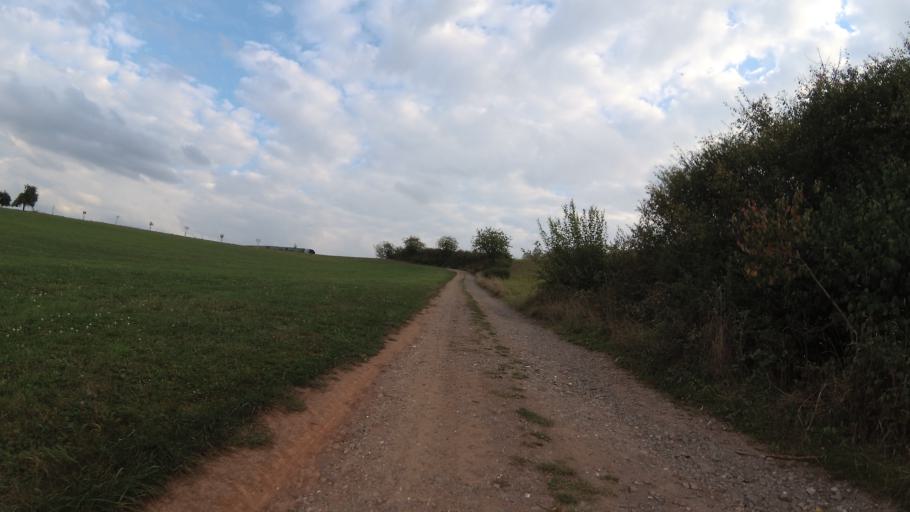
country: DE
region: Saarland
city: Ottweiler
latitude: 49.4198
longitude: 7.1546
